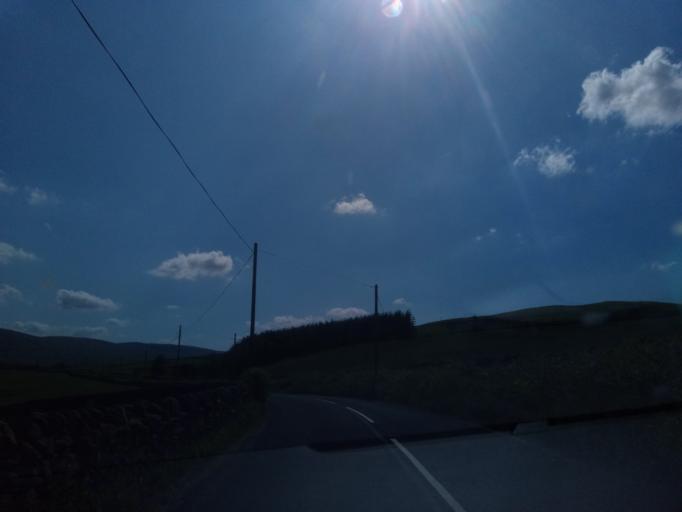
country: GB
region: Scotland
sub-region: The Scottish Borders
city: Innerleithen
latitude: 55.5346
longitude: -3.0361
